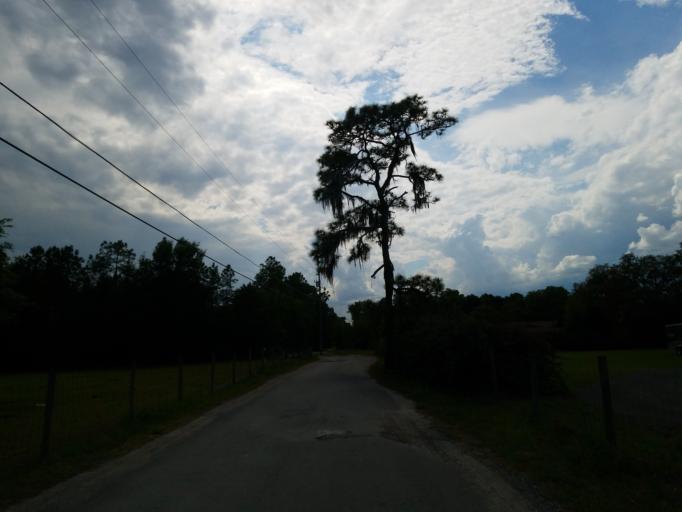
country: US
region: Florida
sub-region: Hernando County
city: Hill 'n Dale
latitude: 28.5300
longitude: -82.2773
